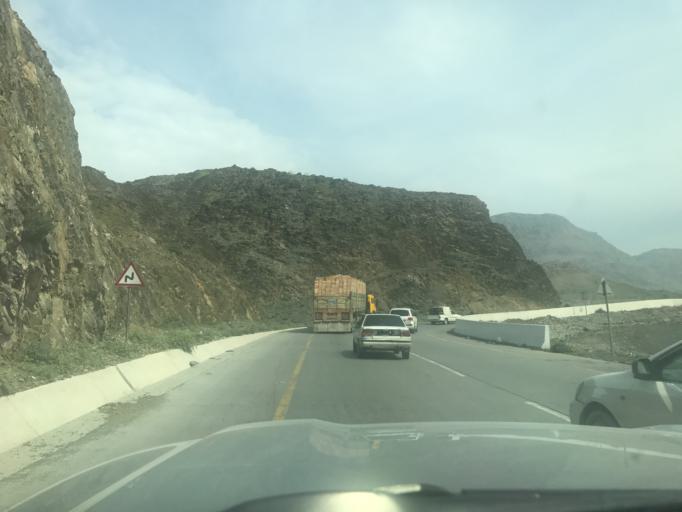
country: PK
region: Federally Administered Tribal Areas
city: Landi Kotal
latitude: 34.0061
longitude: 71.2982
